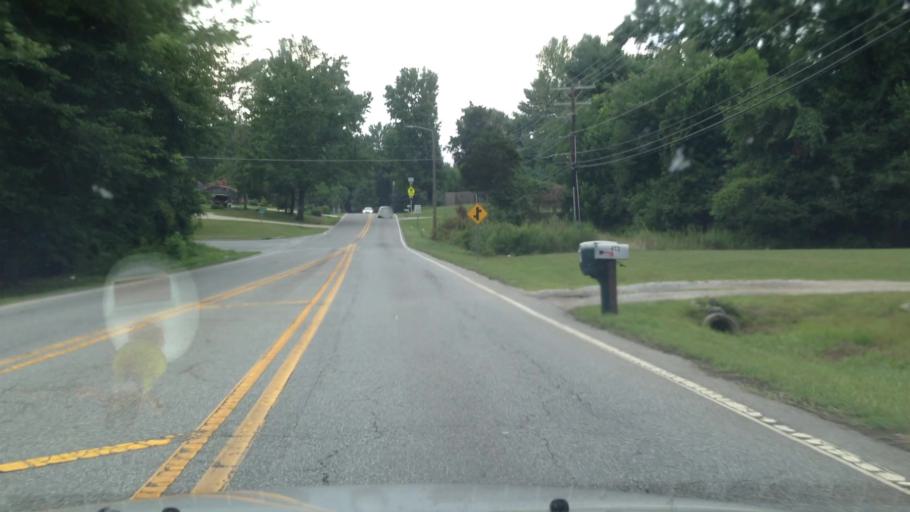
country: US
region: North Carolina
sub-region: Forsyth County
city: Kernersville
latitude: 36.1311
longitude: -80.0708
